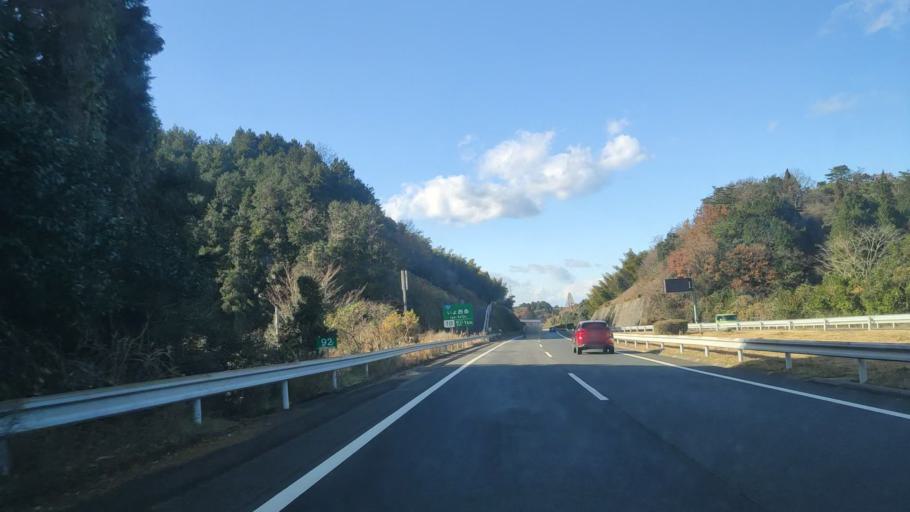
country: JP
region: Ehime
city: Saijo
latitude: 33.9093
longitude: 133.2505
